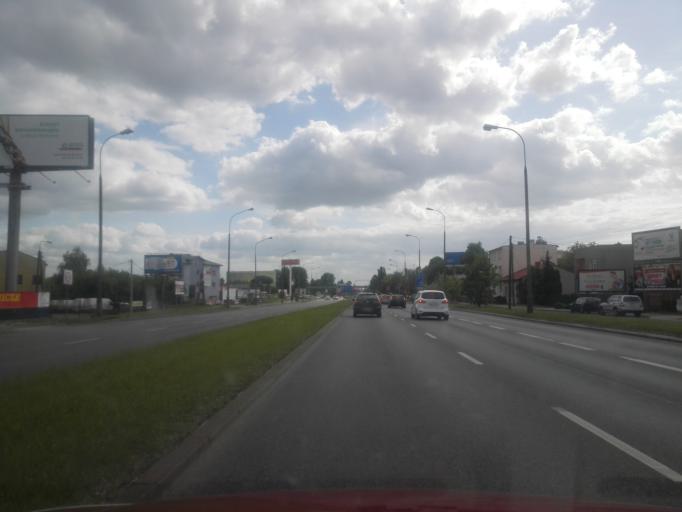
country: PL
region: Masovian Voivodeship
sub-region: Warszawa
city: Targowek
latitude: 52.2784
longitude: 21.0683
